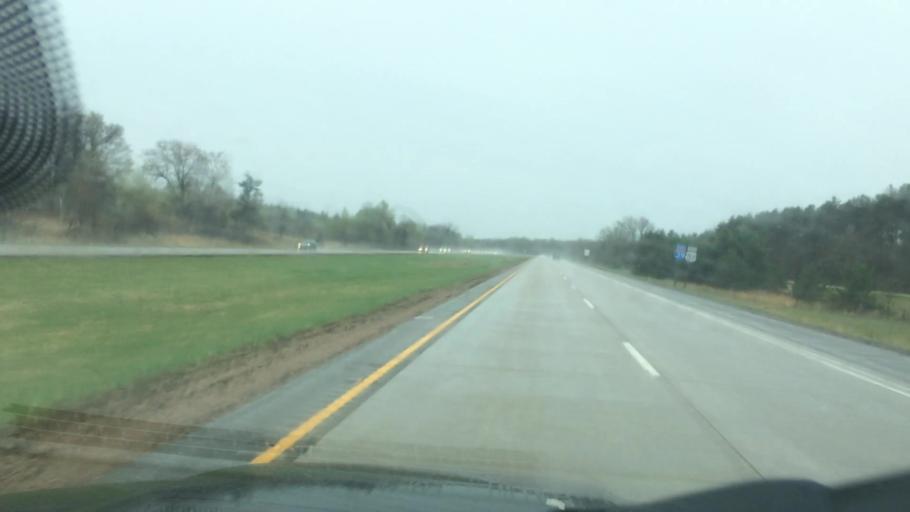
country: US
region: Wisconsin
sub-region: Marathon County
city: Mosinee
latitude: 44.6685
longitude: -89.6427
